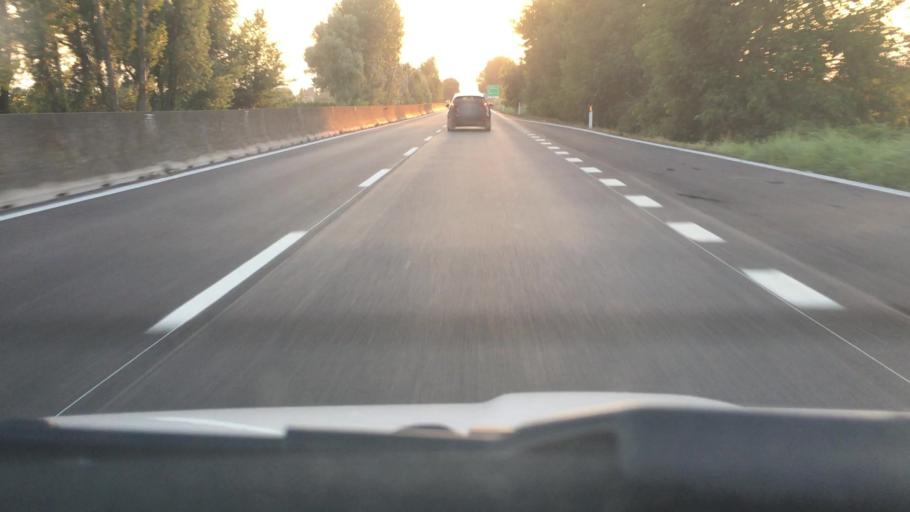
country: IT
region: Emilia-Romagna
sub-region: Provincia di Ferrara
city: Quartesana
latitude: 44.7845
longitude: 11.7469
